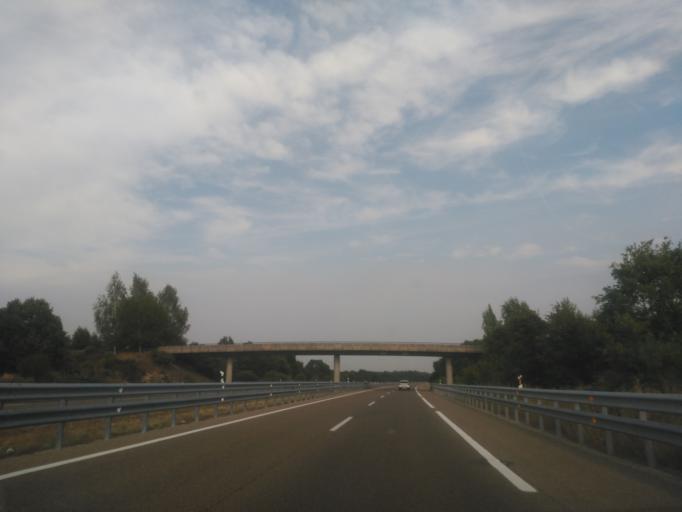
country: ES
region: Castille and Leon
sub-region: Provincia de Zamora
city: Cernadilla
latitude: 42.0381
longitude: -6.4466
